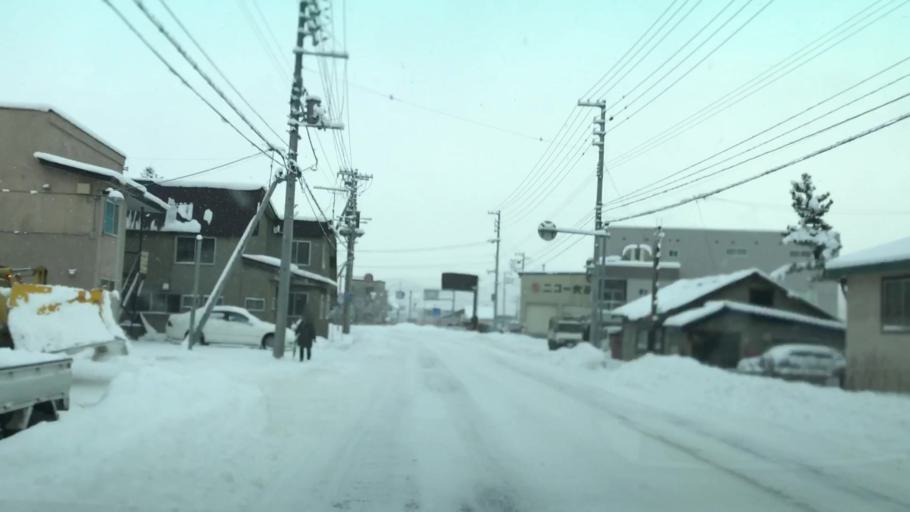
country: JP
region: Hokkaido
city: Yoichi
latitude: 43.2012
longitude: 140.7770
